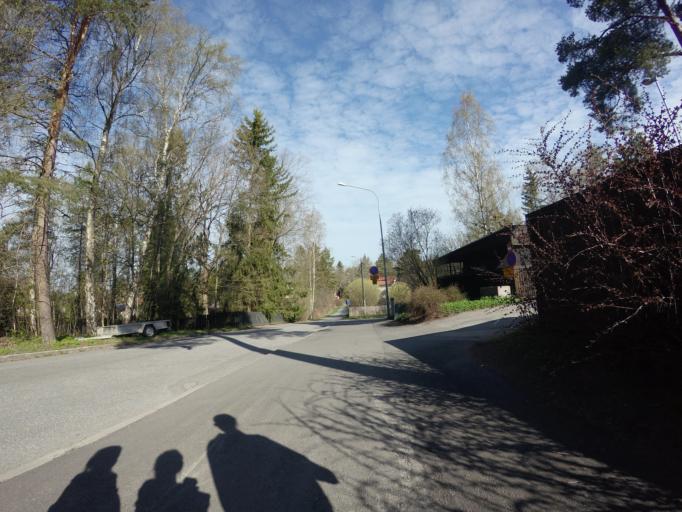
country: FI
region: Varsinais-Suomi
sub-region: Turku
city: Raisio
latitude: 60.4567
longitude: 22.1610
